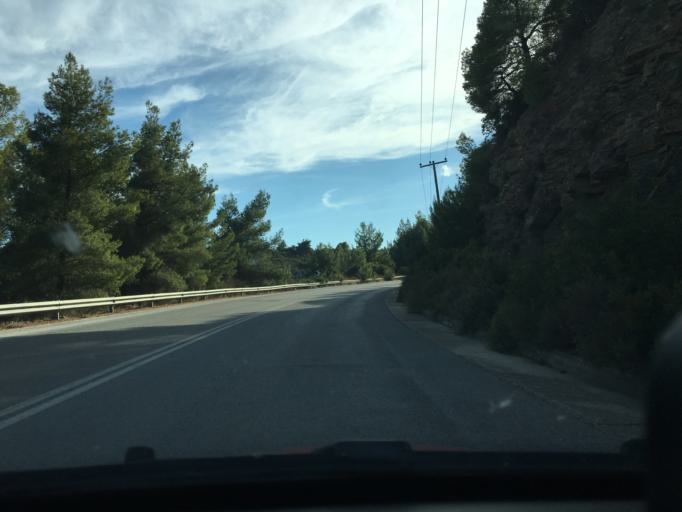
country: GR
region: Central Macedonia
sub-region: Nomos Chalkidikis
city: Agios Nikolaos
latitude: 40.2807
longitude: 23.6852
